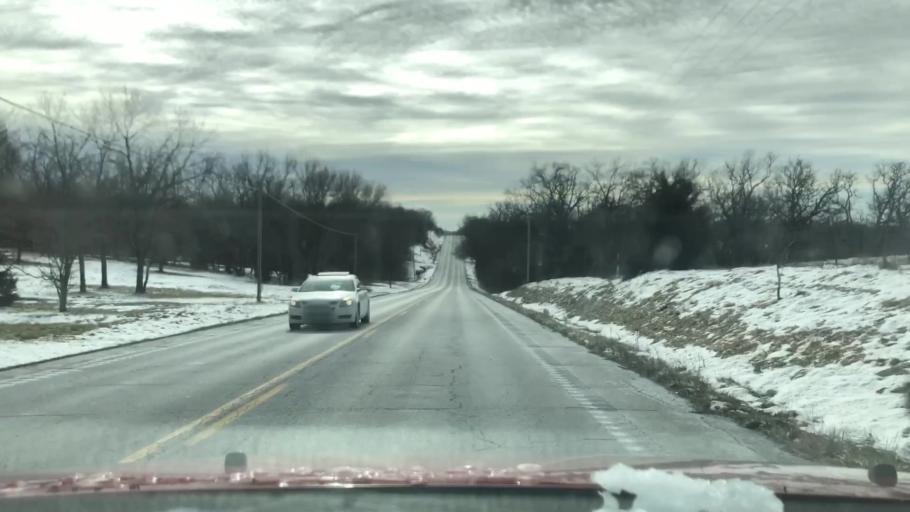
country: US
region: Missouri
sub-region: Jackson County
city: Oak Grove
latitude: 38.9733
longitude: -94.1306
